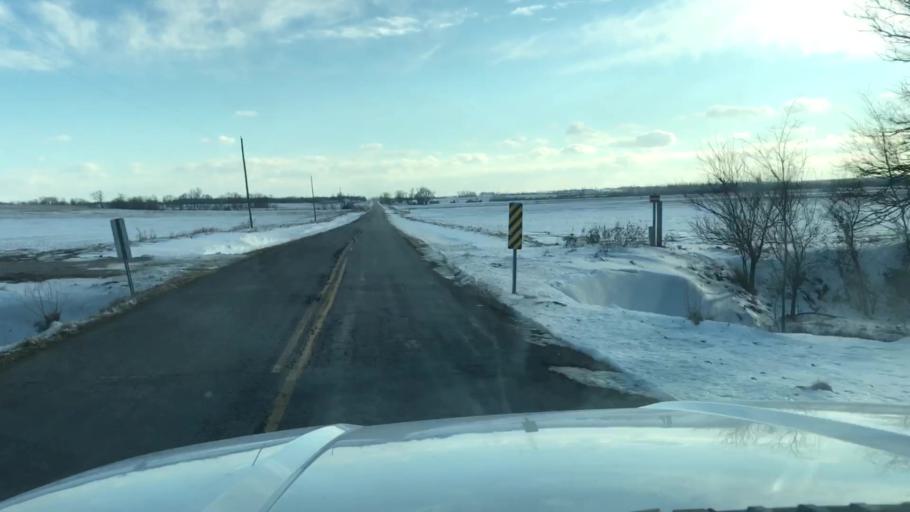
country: US
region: Missouri
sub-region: Holt County
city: Oregon
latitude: 40.1270
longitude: -95.0224
